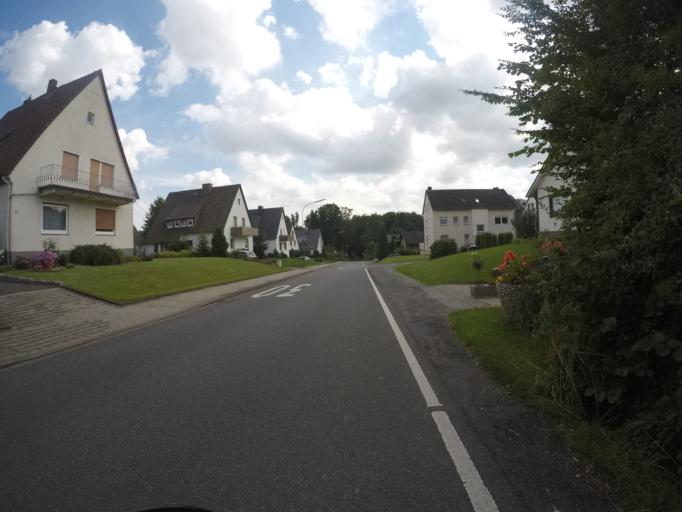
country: DE
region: North Rhine-Westphalia
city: Enger
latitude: 52.1103
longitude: 8.5851
